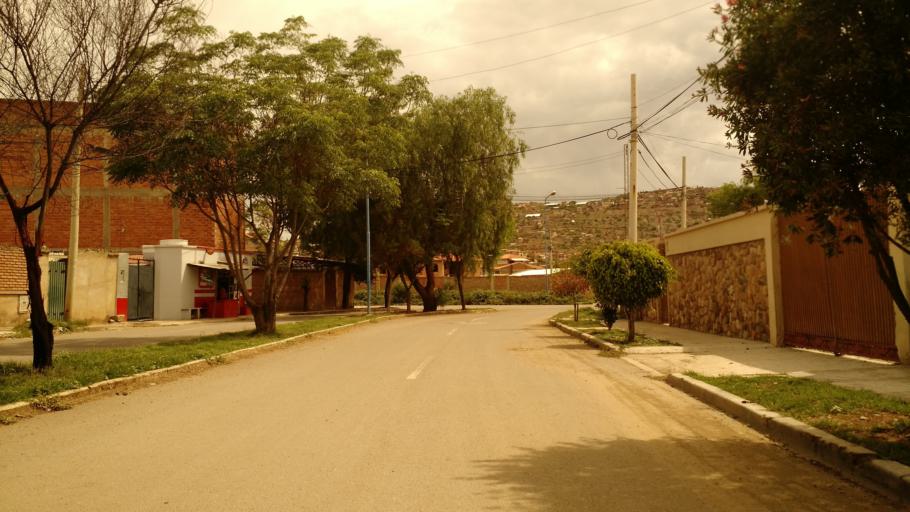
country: BO
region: Cochabamba
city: Cochabamba
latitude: -17.4194
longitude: -66.1248
